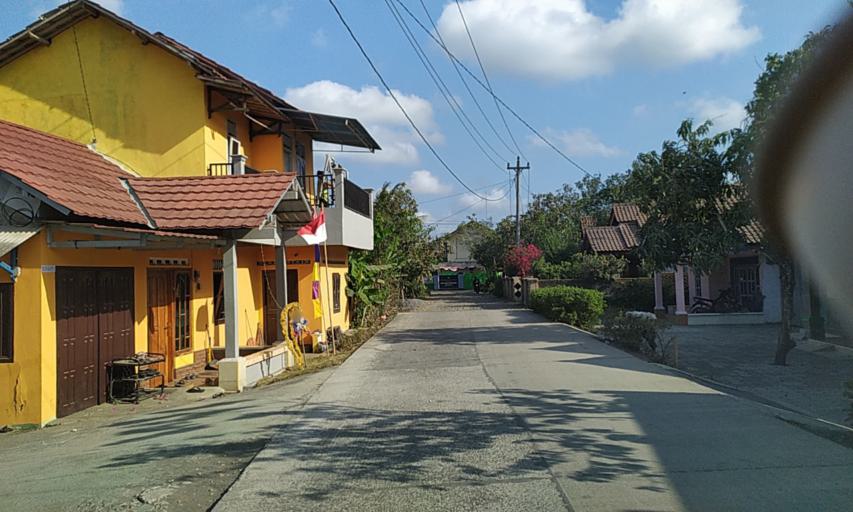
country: ID
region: Central Java
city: Jeruklegi
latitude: -7.6468
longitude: 108.9521
